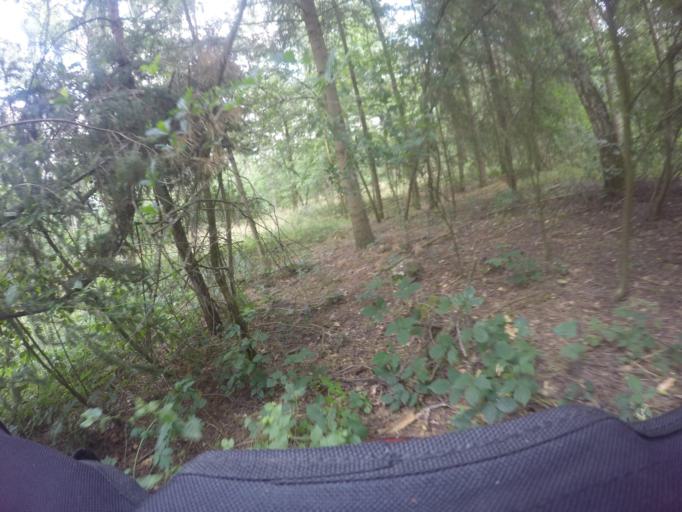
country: DE
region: Lower Saxony
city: Dahlem
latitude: 53.2365
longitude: 10.7452
